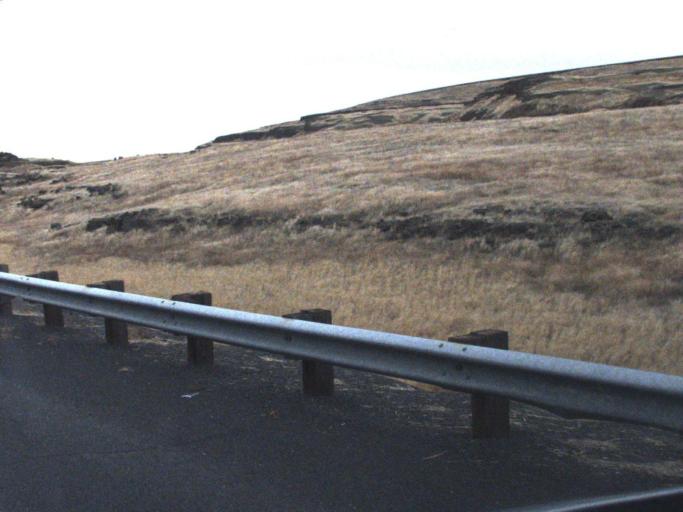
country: US
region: Washington
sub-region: Adams County
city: Ritzville
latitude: 46.7589
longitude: -118.1701
